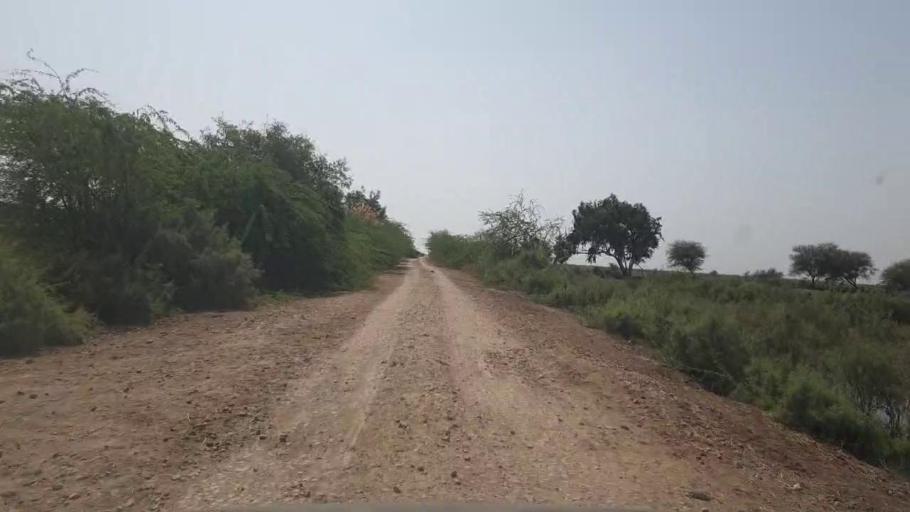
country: PK
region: Sindh
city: Jati
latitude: 24.3796
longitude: 68.6020
